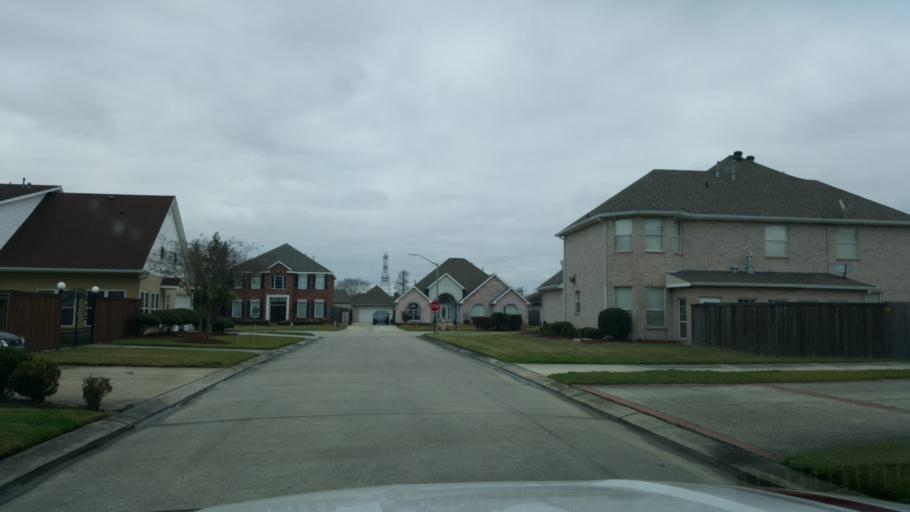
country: US
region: Louisiana
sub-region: Jefferson Parish
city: Woodmere
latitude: 29.8777
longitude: -90.0796
